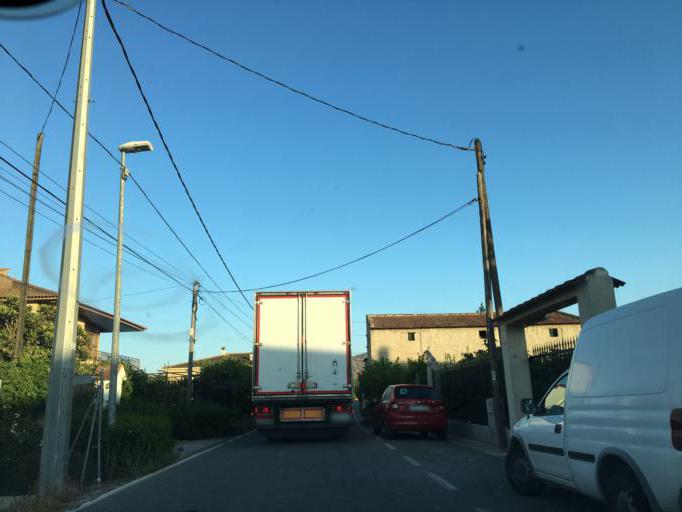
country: ES
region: Murcia
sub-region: Murcia
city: Santomera
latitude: 38.0136
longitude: -1.0567
